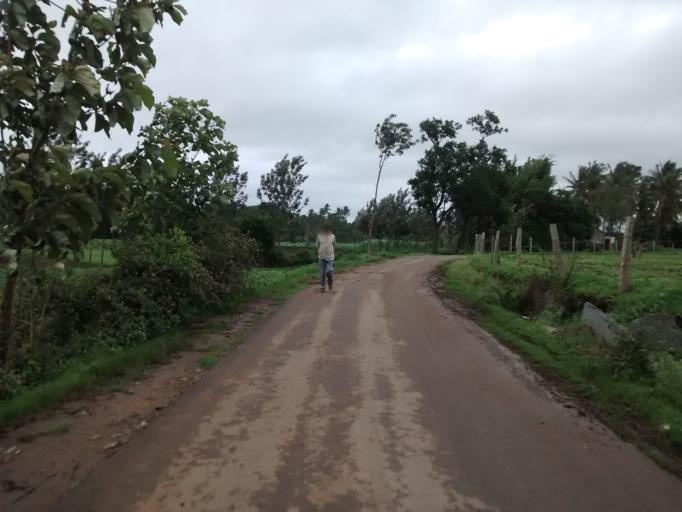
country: IN
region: Karnataka
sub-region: Hassan
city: Hassan
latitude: 12.9287
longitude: 76.1830
